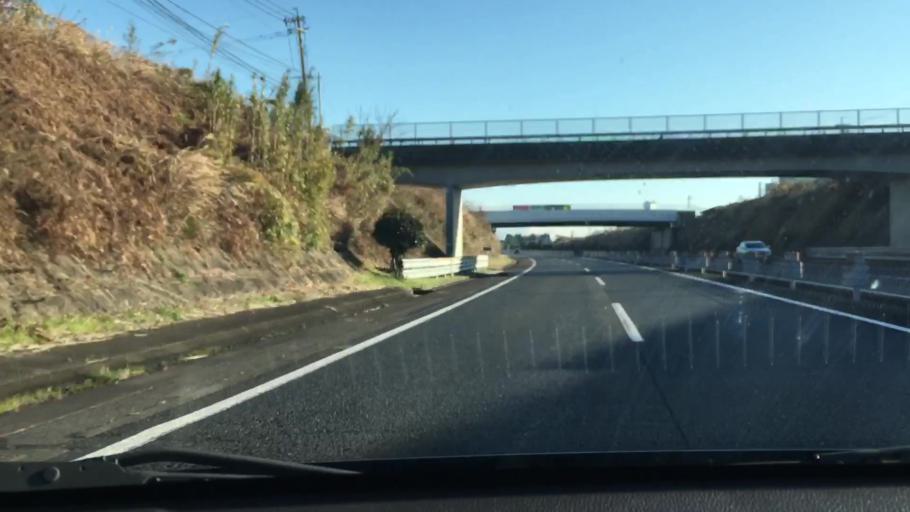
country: JP
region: Kagoshima
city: Kajiki
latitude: 31.8057
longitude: 130.7091
